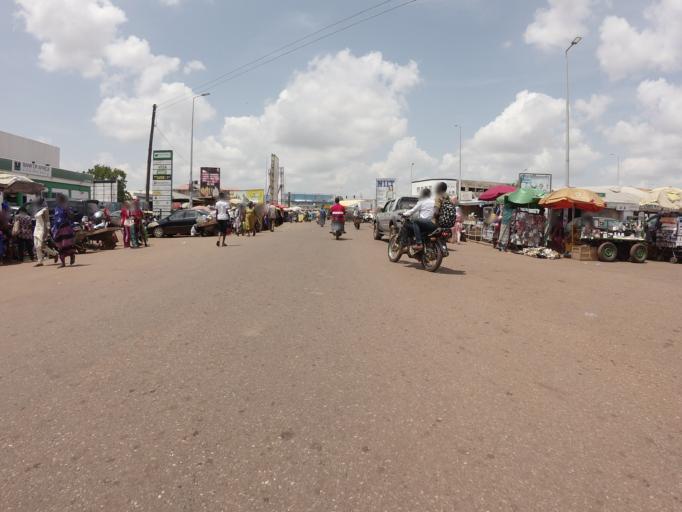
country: GH
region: Northern
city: Tamale
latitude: 9.4034
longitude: -0.8425
